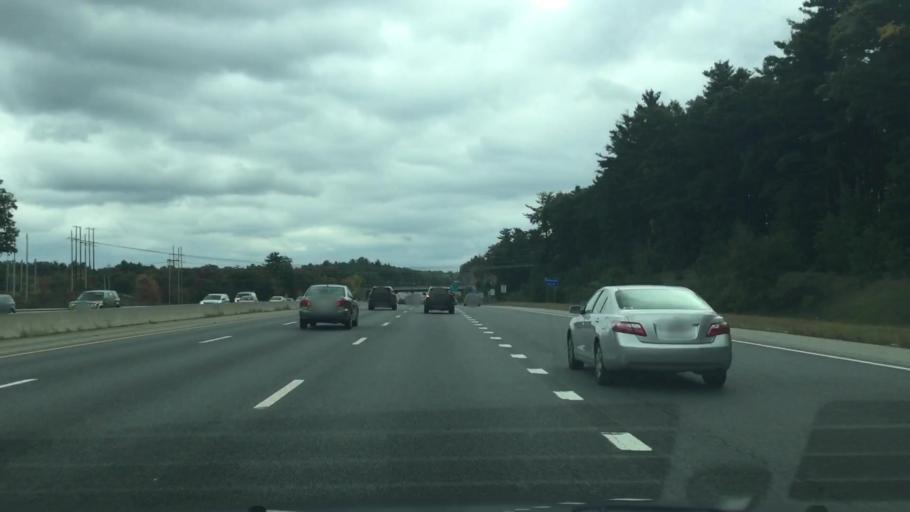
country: US
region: Massachusetts
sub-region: Middlesex County
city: Lowell
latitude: 42.6006
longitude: -71.3211
